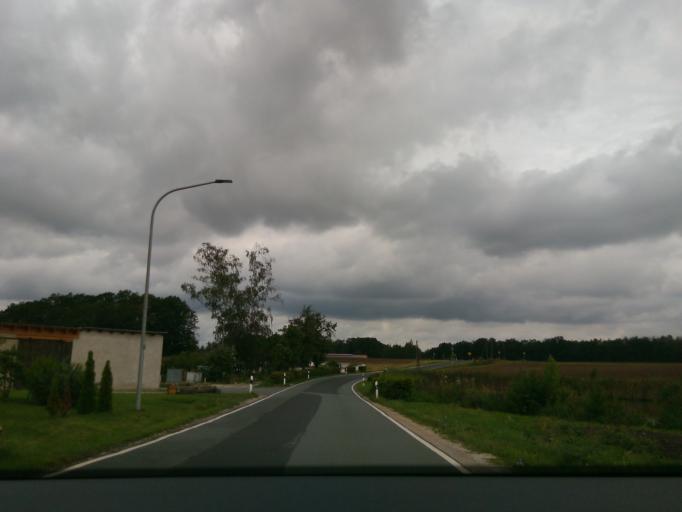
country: DE
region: Bavaria
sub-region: Regierungsbezirk Mittelfranken
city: Hochstadt an der Aisch
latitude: 49.6767
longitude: 10.8080
